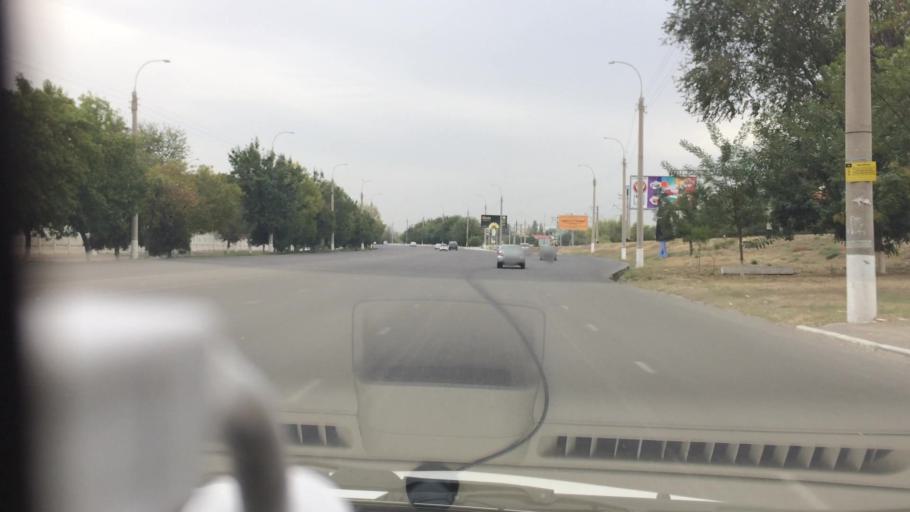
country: UZ
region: Toshkent
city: Salor
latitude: 41.3154
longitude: 69.3097
